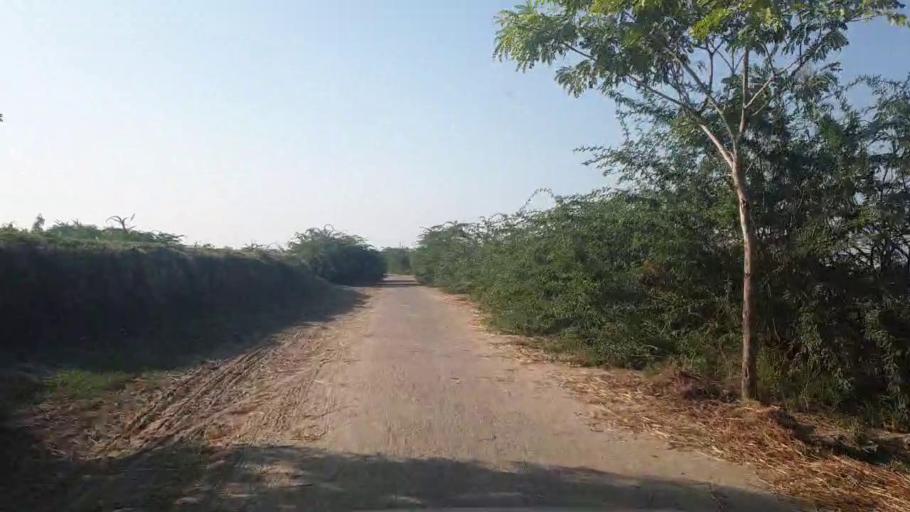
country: PK
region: Sindh
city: Tando Bago
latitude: 24.7420
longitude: 68.9306
